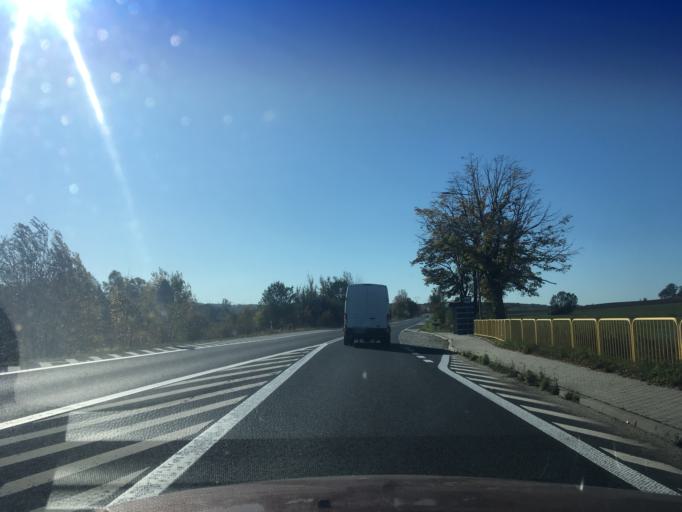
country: DE
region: Saxony
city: Ostritz
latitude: 51.0336
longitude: 14.9716
